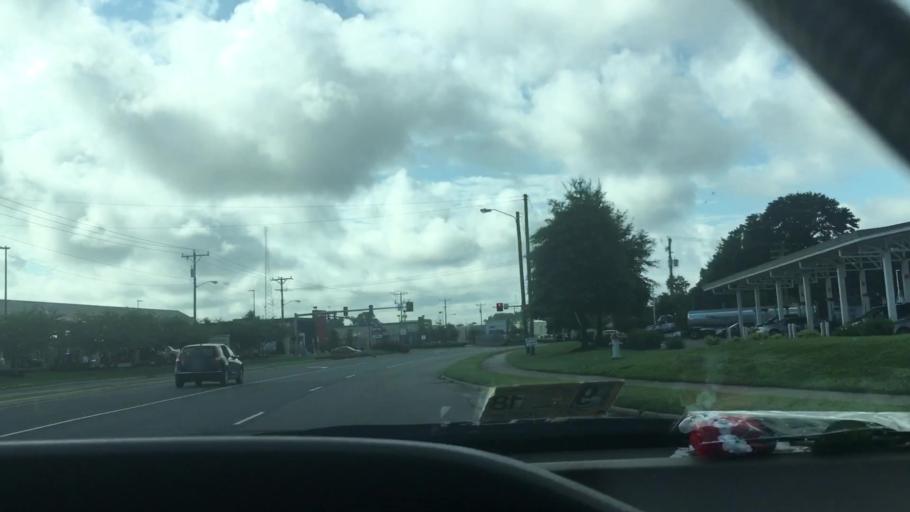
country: US
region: Virginia
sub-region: City of Portsmouth
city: Portsmouth Heights
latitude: 36.8288
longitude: -76.3389
